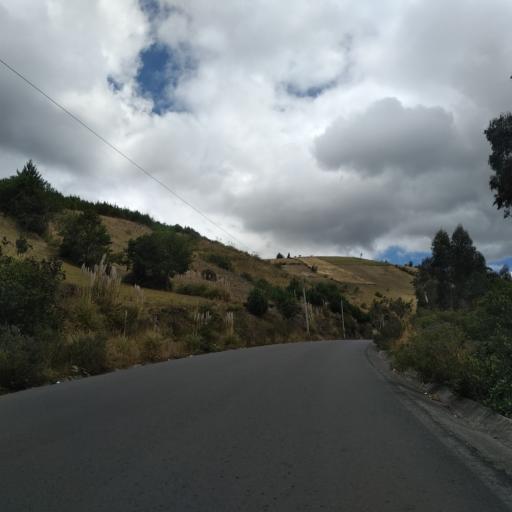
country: EC
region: Cotopaxi
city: Saquisili
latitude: -0.7505
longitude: -78.7236
